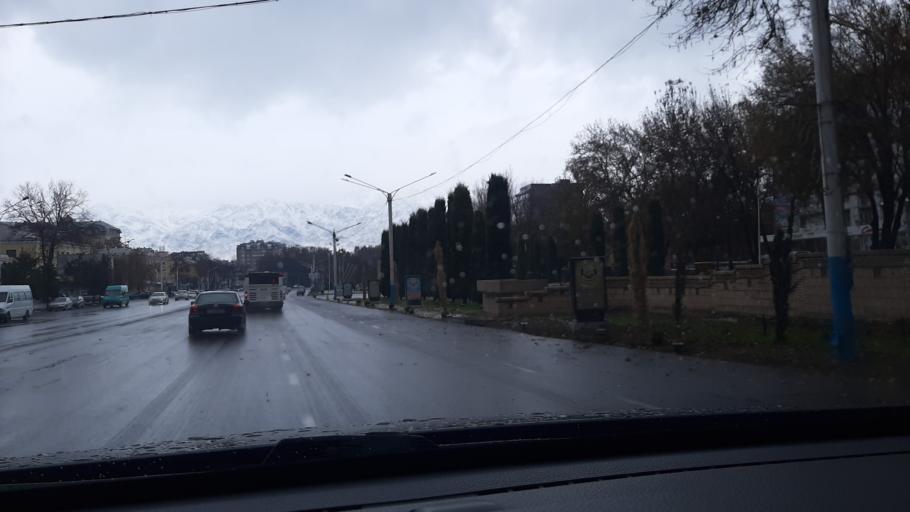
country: TJ
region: Viloyati Sughd
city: Khujand
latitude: 40.2825
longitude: 69.6244
